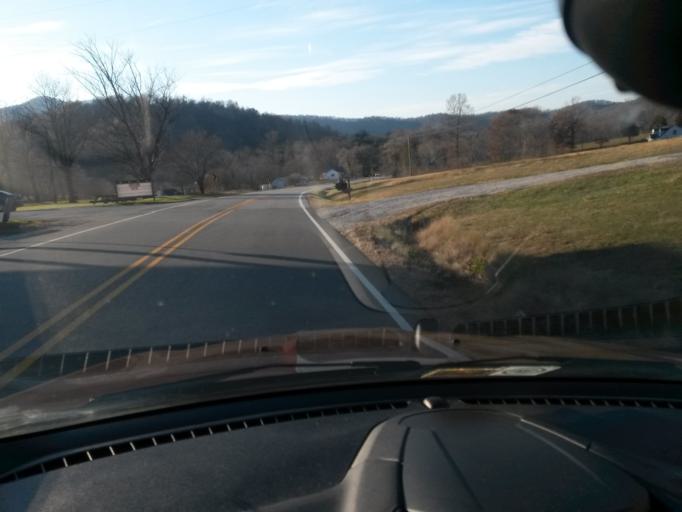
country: US
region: Virginia
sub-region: Amherst County
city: Amherst
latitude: 37.6232
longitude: -79.1115
